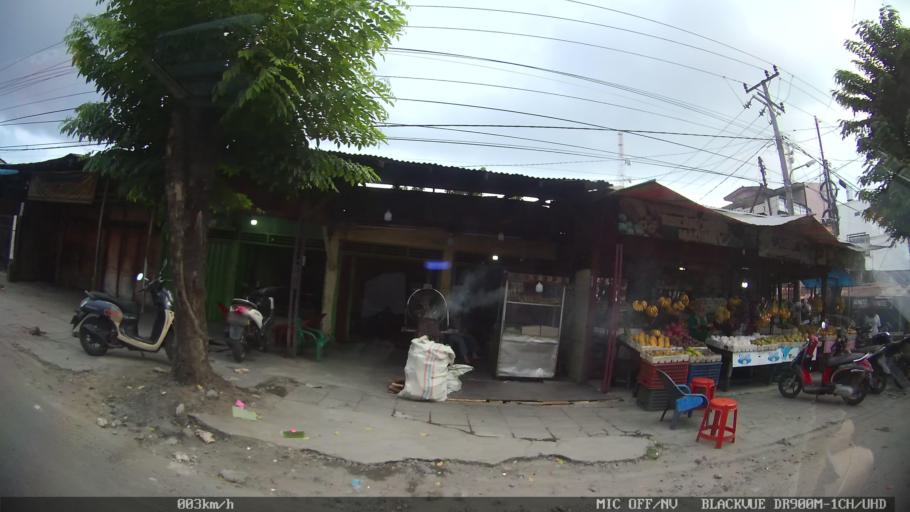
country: ID
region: North Sumatra
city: Medan
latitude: 3.5972
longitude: 98.7281
